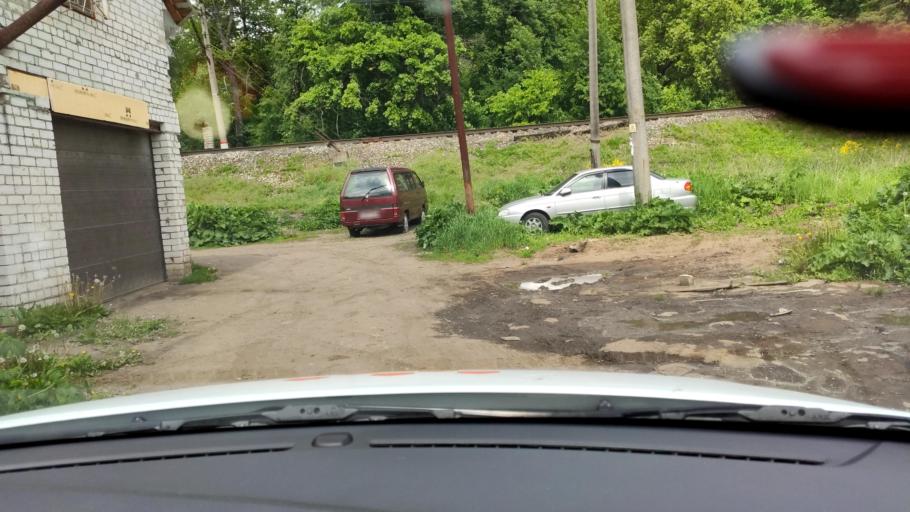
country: RU
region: Tatarstan
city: Staroye Arakchino
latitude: 55.8016
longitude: 48.9840
